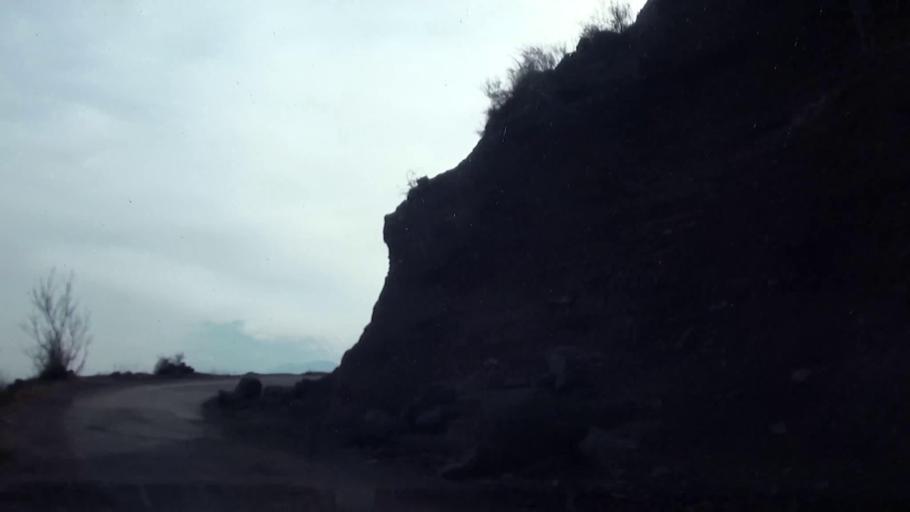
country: PK
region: Azad Kashmir
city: Muzaffarabad
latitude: 34.3686
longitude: 73.5217
